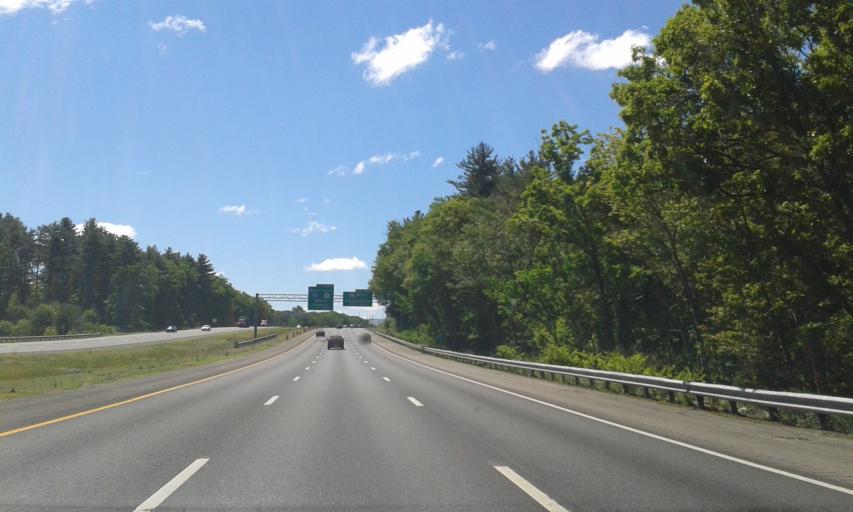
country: US
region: Massachusetts
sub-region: Middlesex County
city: Burlington
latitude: 42.4874
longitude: -71.2288
